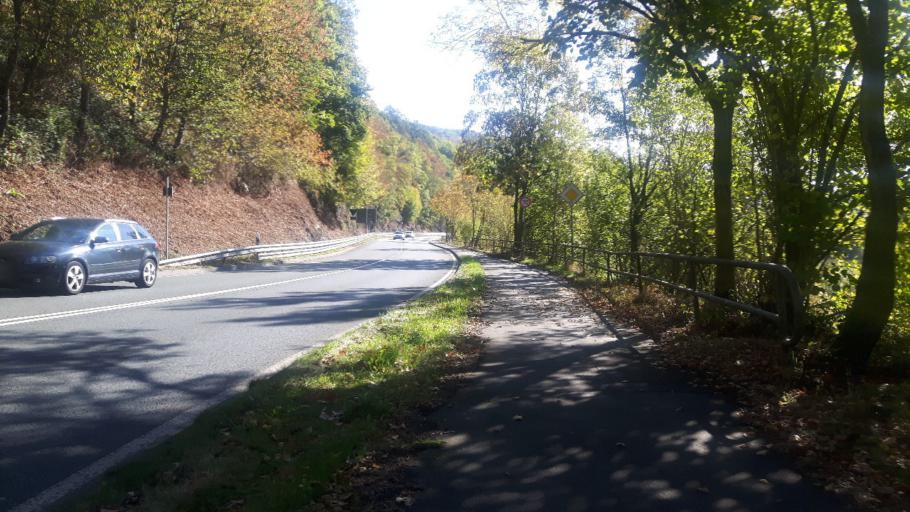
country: DE
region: Rheinland-Pfalz
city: Niederirsen
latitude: 50.8119
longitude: 7.6039
